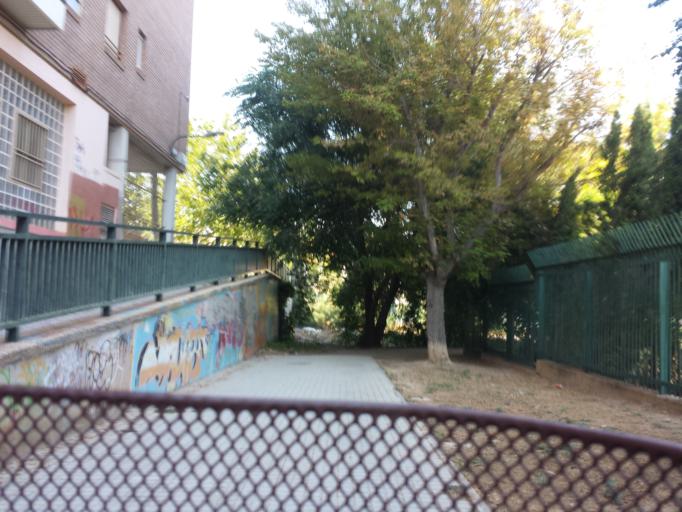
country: ES
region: Aragon
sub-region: Provincia de Zaragoza
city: Zaragoza
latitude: 41.6349
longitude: -0.8731
